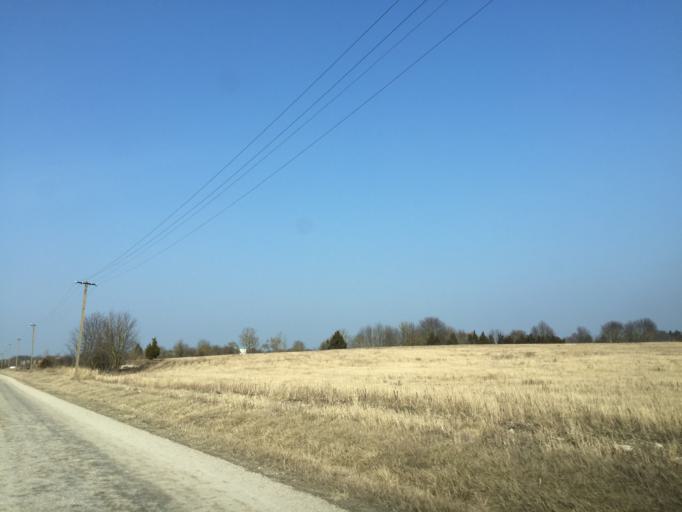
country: EE
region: Saare
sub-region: Orissaare vald
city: Orissaare
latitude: 58.4933
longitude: 23.1168
